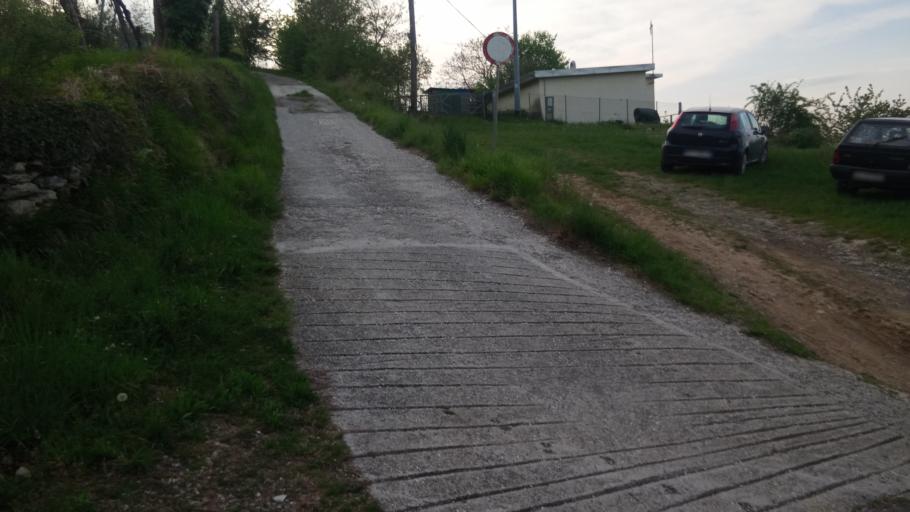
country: IT
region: Veneto
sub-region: Provincia di Vicenza
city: Conco
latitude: 45.7770
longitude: 11.6083
